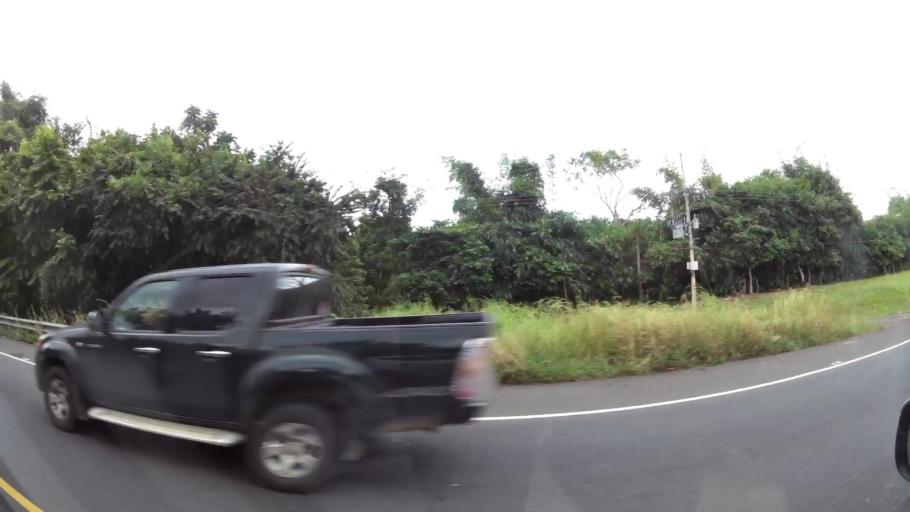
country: CR
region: Alajuela
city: Orotina
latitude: 9.8935
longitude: -84.6213
